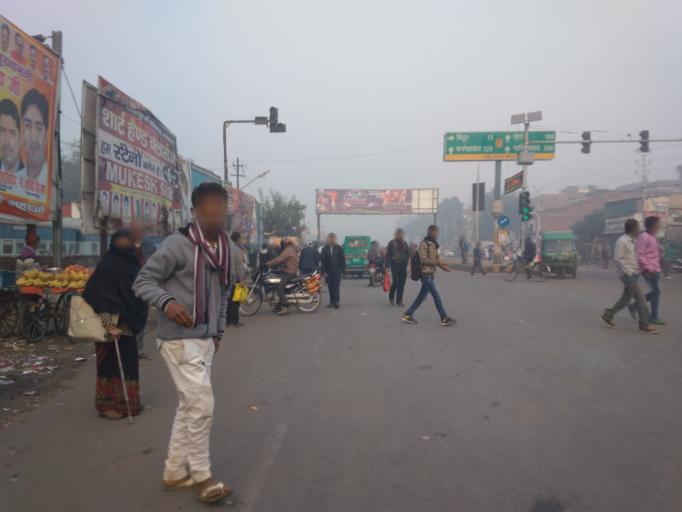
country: IN
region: Uttar Pradesh
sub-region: Kanpur
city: Nawabganj
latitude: 26.5031
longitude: 80.2530
